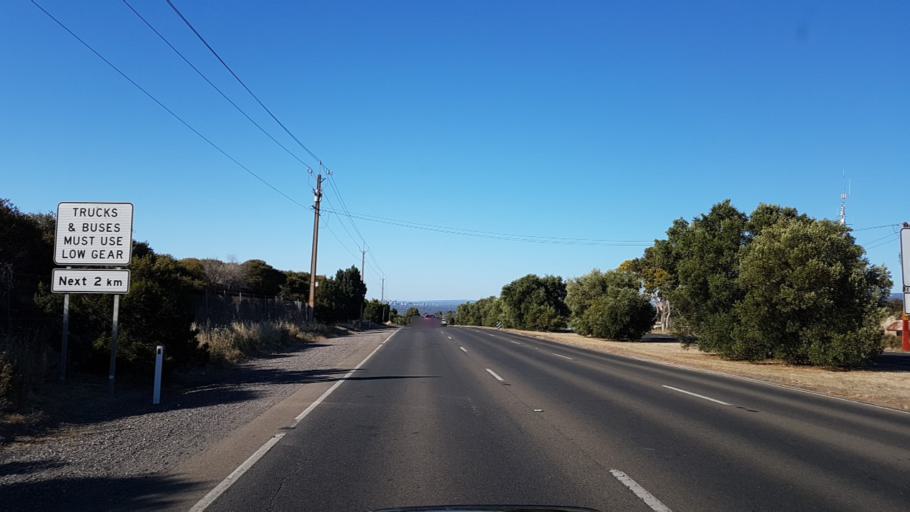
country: AU
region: South Australia
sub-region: Onkaparinga
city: Bedford Park
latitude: -35.0481
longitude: 138.5597
